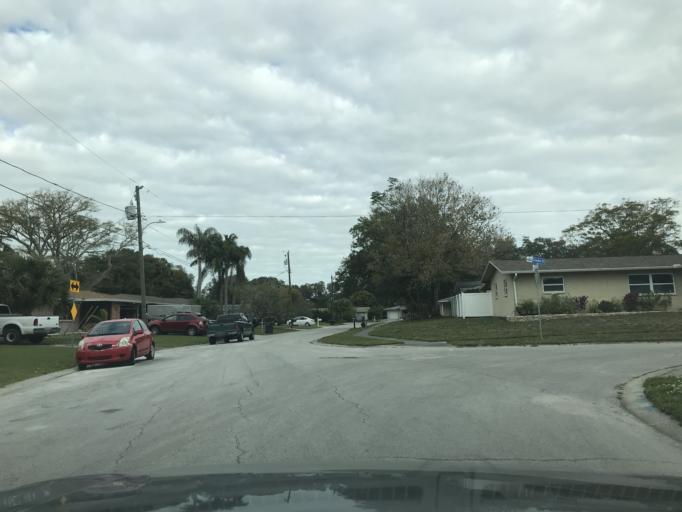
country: US
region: Florida
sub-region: Pinellas County
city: Largo
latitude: 27.9335
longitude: -82.7786
